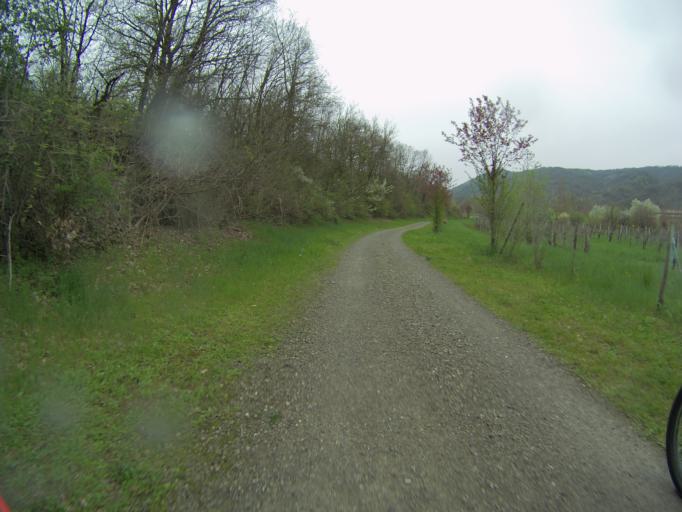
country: IT
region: Emilia-Romagna
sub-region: Provincia di Reggio Emilia
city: Ciano d'Enza
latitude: 44.5822
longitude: 10.4044
